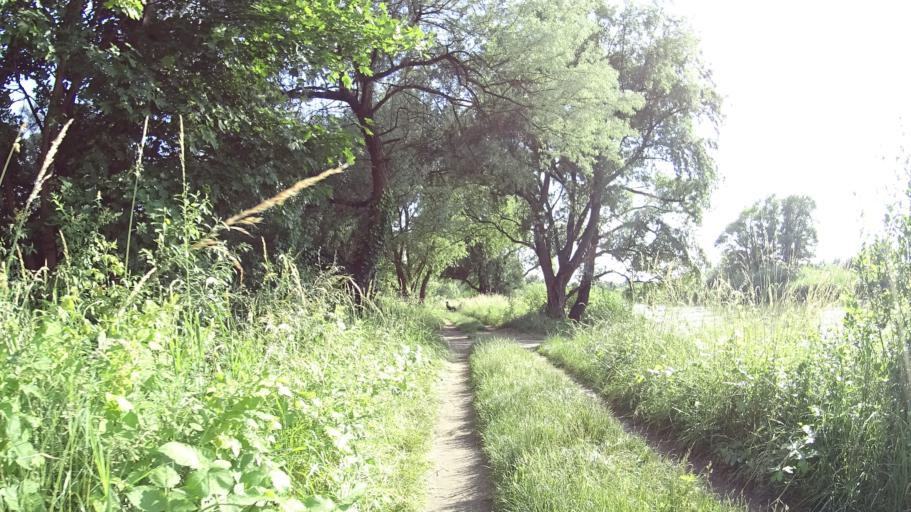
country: HU
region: Pest
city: Dunaharaszti
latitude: 47.3637
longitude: 19.0874
